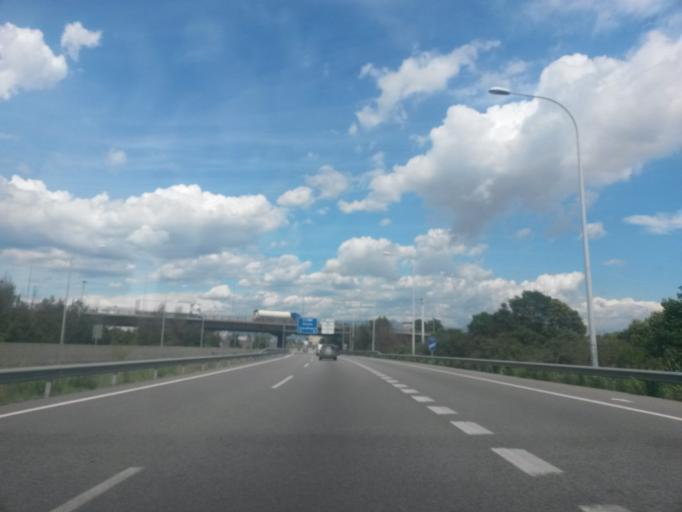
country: ES
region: Catalonia
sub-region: Provincia de Barcelona
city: Montmelo
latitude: 41.5476
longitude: 2.2351
